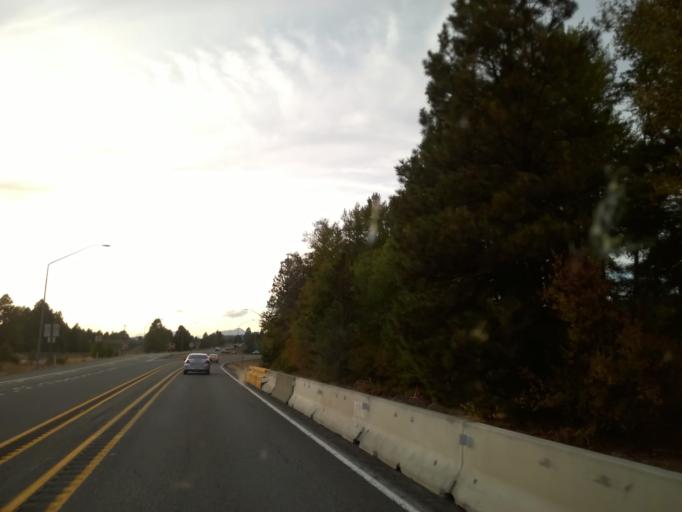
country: US
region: Washington
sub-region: Kittitas County
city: Cle Elum
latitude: 47.1860
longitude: -120.8952
